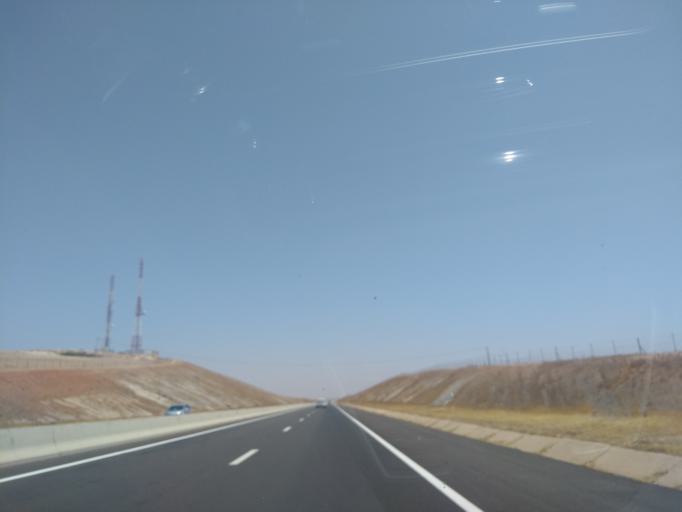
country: MA
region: Marrakech-Tensift-Al Haouz
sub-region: Kelaa-Des-Sraghna
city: Sidi Abdallah
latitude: 32.3078
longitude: -7.9589
